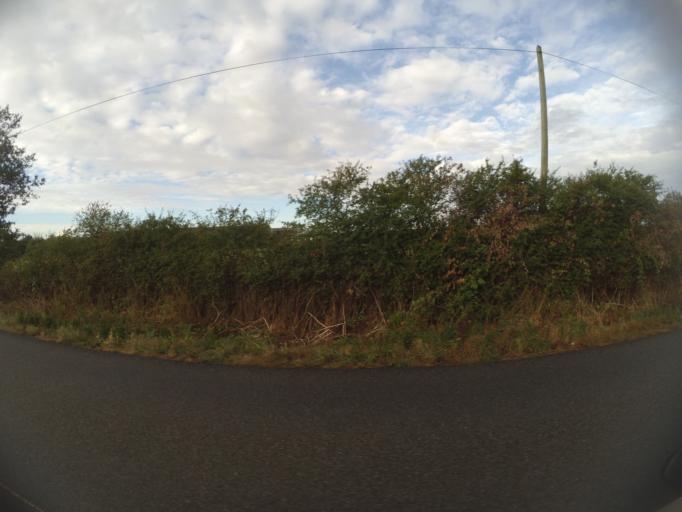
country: FR
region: Pays de la Loire
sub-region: Departement de la Loire-Atlantique
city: Saint-Lumine-de-Clisson
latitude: 47.0770
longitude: -1.3288
